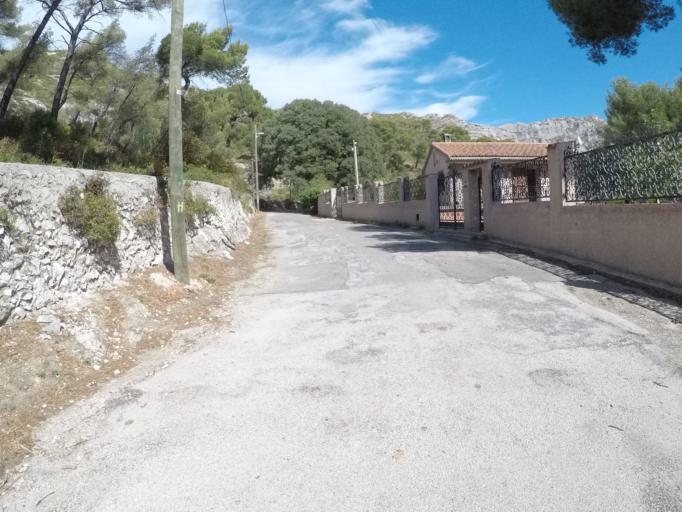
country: FR
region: Provence-Alpes-Cote d'Azur
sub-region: Departement des Bouches-du-Rhone
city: Marseille 09
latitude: 43.2484
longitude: 5.4364
